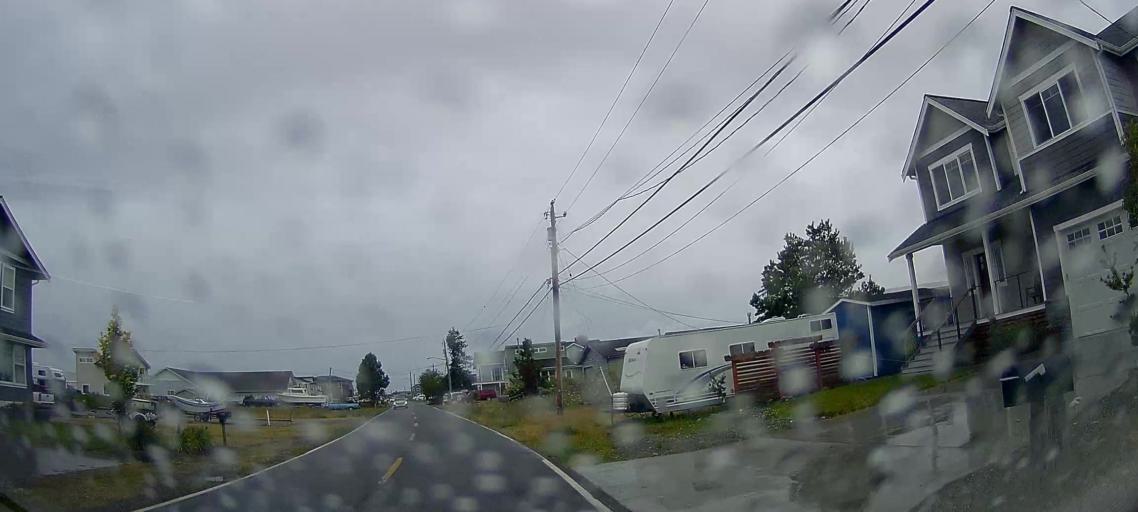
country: US
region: Washington
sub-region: Whatcom County
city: Ferndale
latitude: 48.7970
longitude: -122.7051
